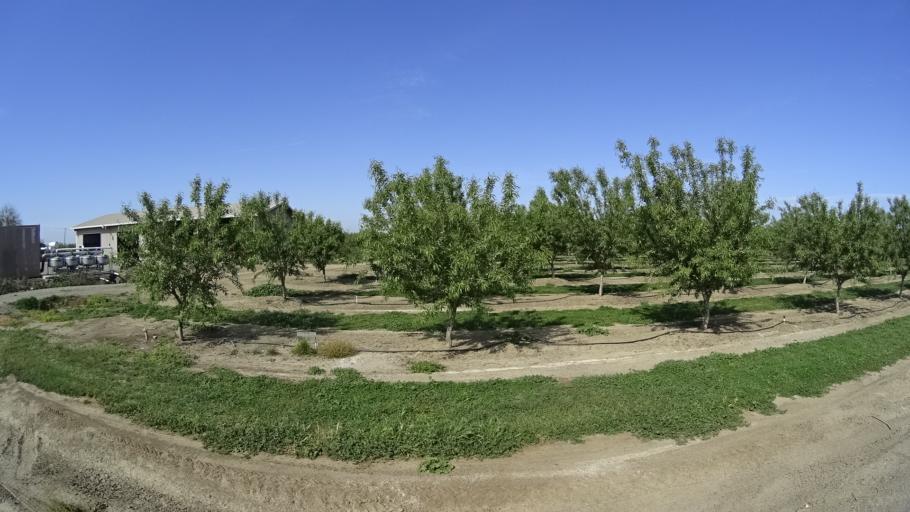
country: US
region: California
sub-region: Glenn County
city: Hamilton City
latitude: 39.6536
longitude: -122.0180
